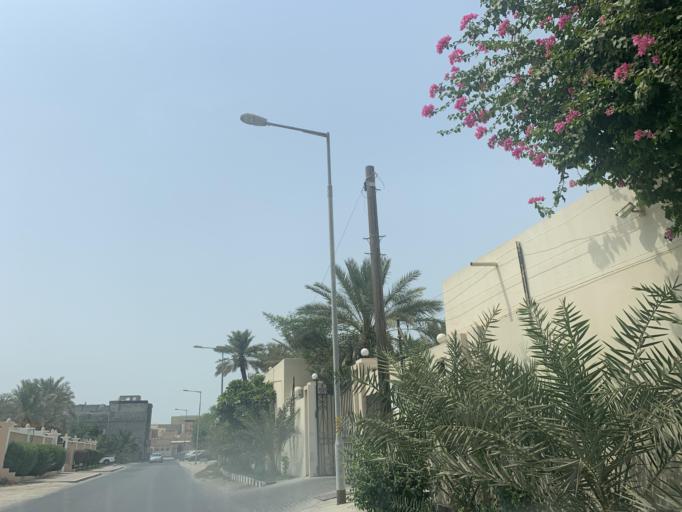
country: BH
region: Northern
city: Madinat `Isa
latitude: 26.1955
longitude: 50.4666
